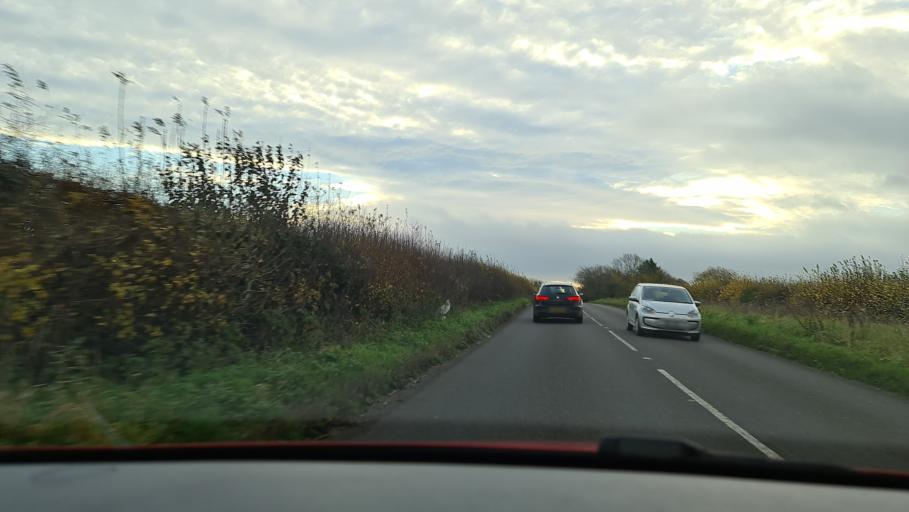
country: GB
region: England
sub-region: Oxfordshire
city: Bicester
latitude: 51.8722
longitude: -1.1067
